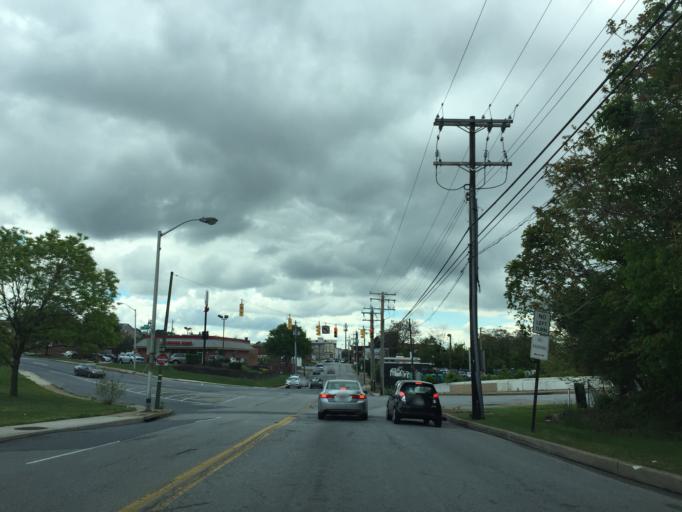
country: US
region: Maryland
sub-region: City of Baltimore
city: Baltimore
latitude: 39.3213
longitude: -76.6271
